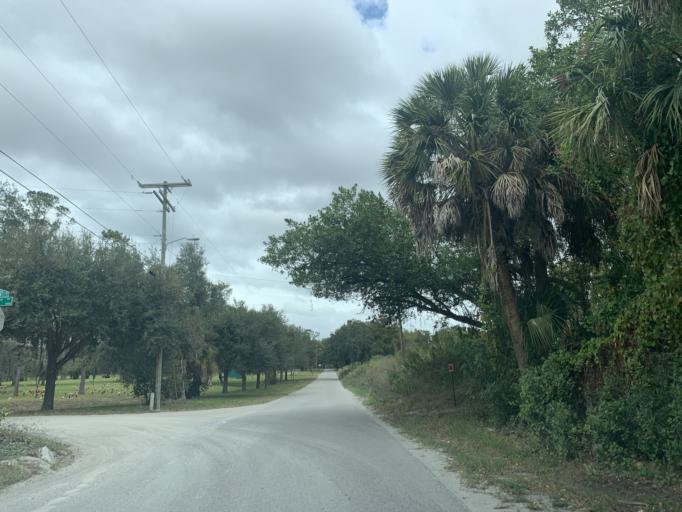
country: US
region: Florida
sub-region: Hillsborough County
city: East Lake-Orient Park
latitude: 27.9758
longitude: -82.4058
